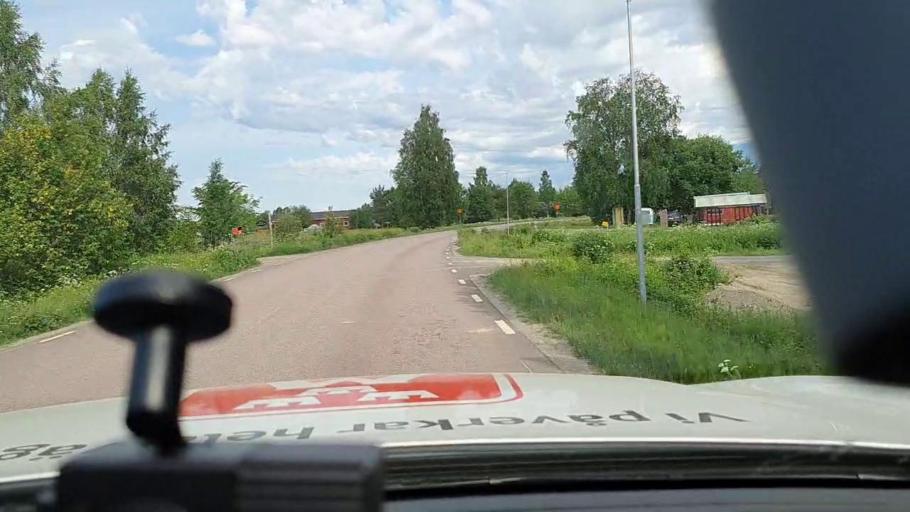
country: SE
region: Norrbotten
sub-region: Bodens Kommun
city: Saevast
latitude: 65.6856
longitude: 21.7865
